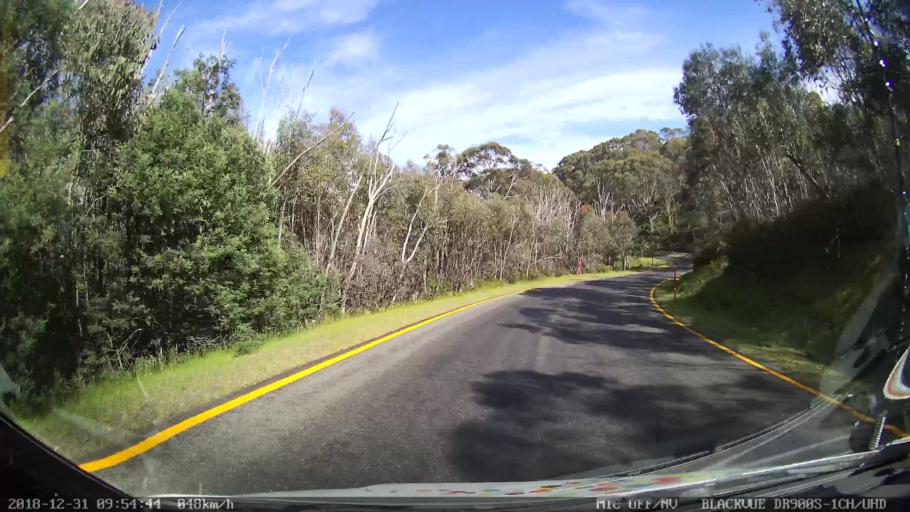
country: AU
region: New South Wales
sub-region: Snowy River
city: Jindabyne
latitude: -36.5343
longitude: 148.2337
